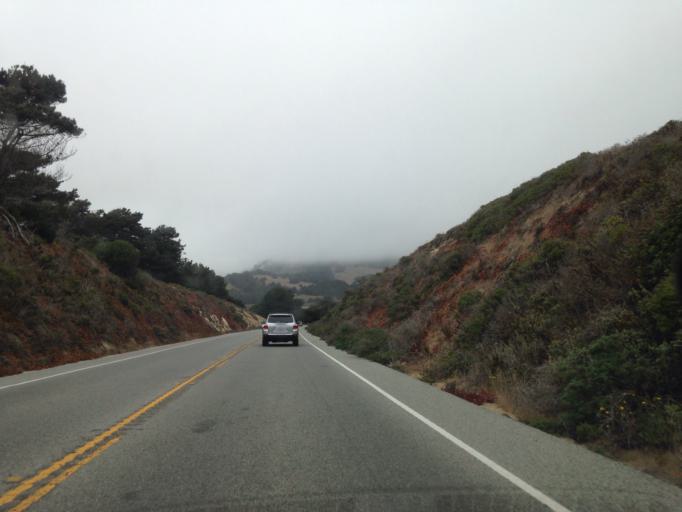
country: US
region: California
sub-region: San Mateo County
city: Half Moon Bay
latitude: 37.3165
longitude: -122.4033
